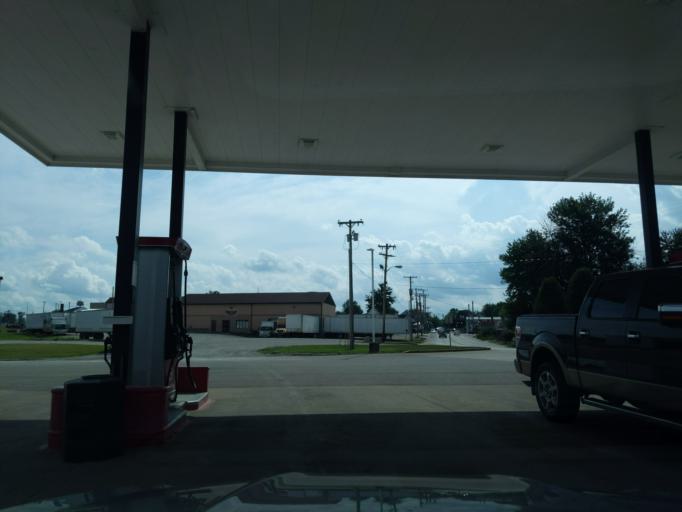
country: US
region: Indiana
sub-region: Ripley County
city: Osgood
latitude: 39.1326
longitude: -85.2902
